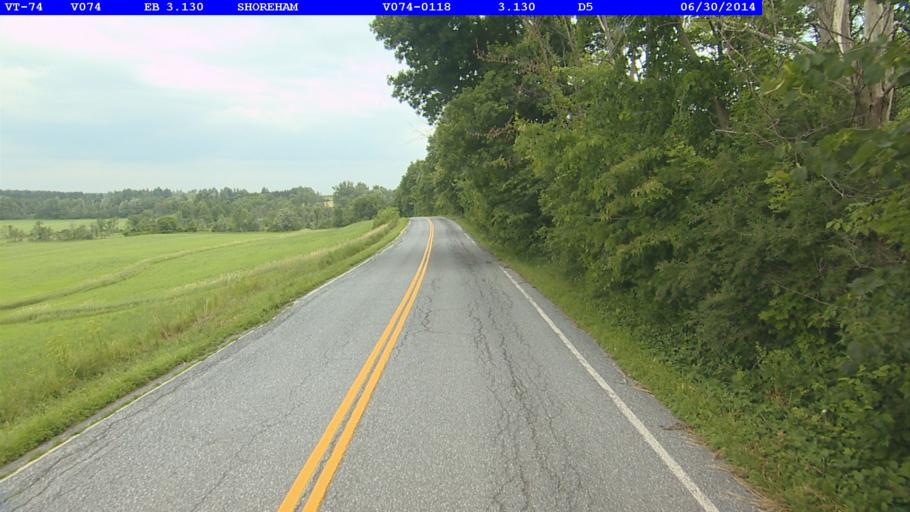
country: US
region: New York
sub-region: Essex County
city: Ticonderoga
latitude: 43.8769
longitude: -73.3332
